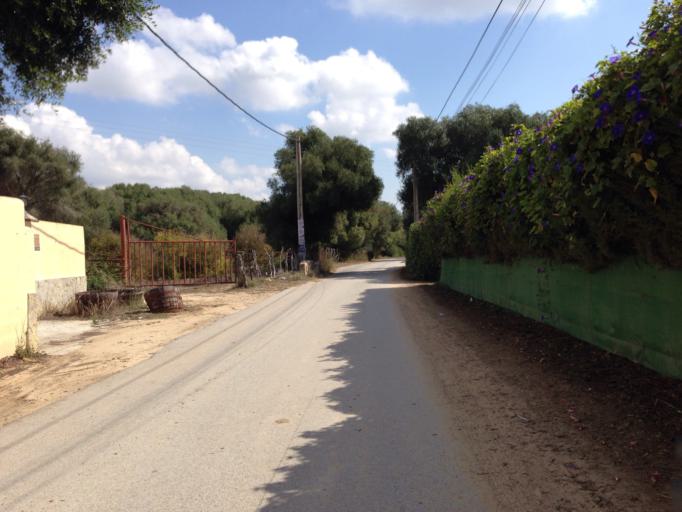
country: ES
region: Andalusia
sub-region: Provincia de Cadiz
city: Vejer de la Frontera
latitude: 36.2078
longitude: -6.0381
